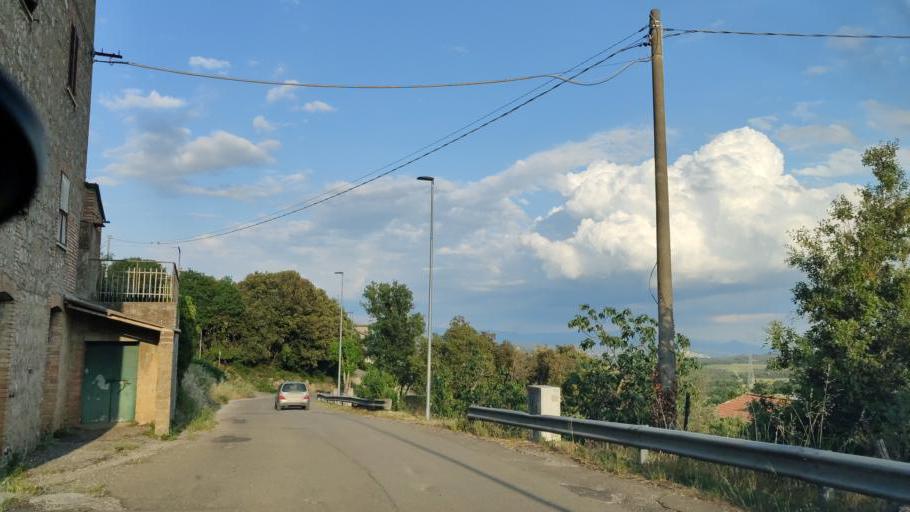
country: IT
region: Umbria
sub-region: Provincia di Terni
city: Lugnano in Teverina
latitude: 42.5991
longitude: 12.3629
